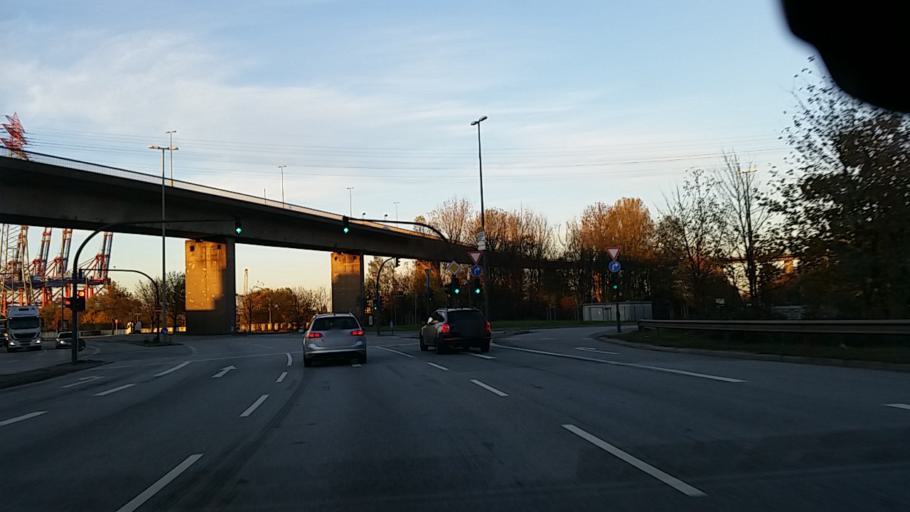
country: DE
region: Hamburg
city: Altona
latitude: 53.5179
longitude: 9.9275
